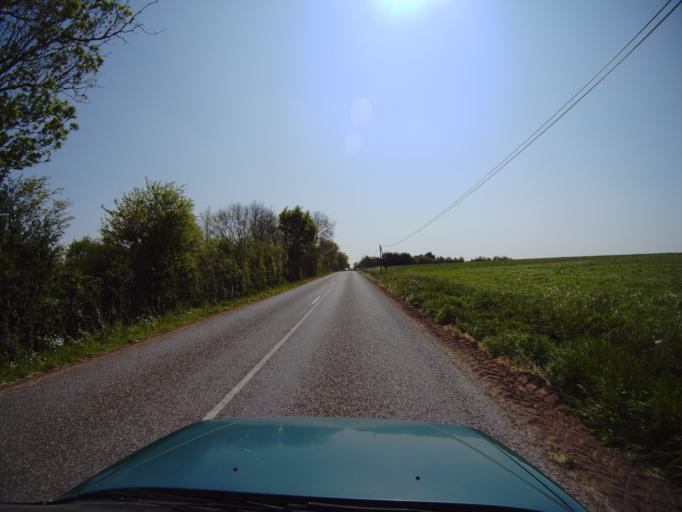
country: FR
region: Pays de la Loire
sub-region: Departement de la Vendee
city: Saint-Andre-Treize-Voies
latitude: 46.9503
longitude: -1.4165
